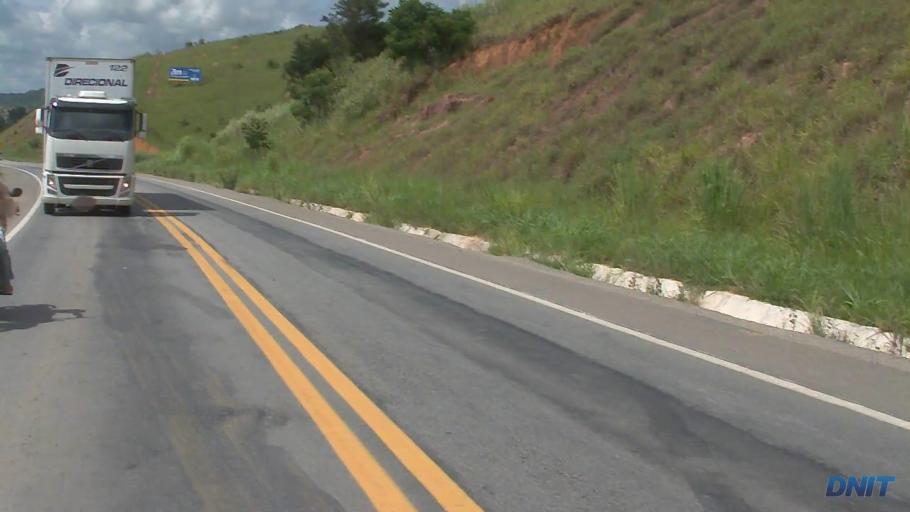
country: BR
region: Minas Gerais
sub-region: Governador Valadares
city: Governador Valadares
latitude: -19.0431
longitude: -42.1506
